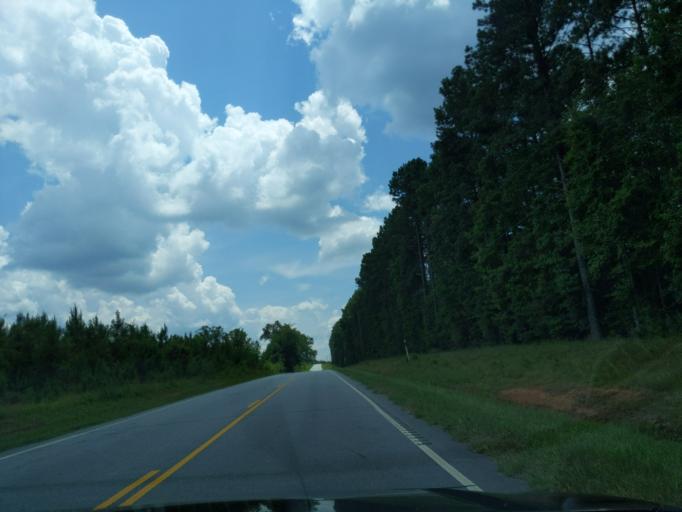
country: US
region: South Carolina
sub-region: Greenwood County
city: Ninety Six
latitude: 34.0211
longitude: -82.0405
